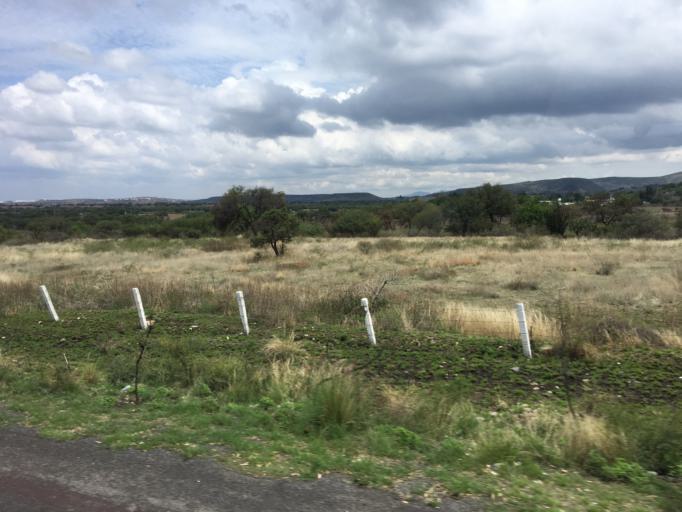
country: MX
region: Guanajuato
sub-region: Silao de la Victoria
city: Aguas Buenas
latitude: 20.9566
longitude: -101.3669
